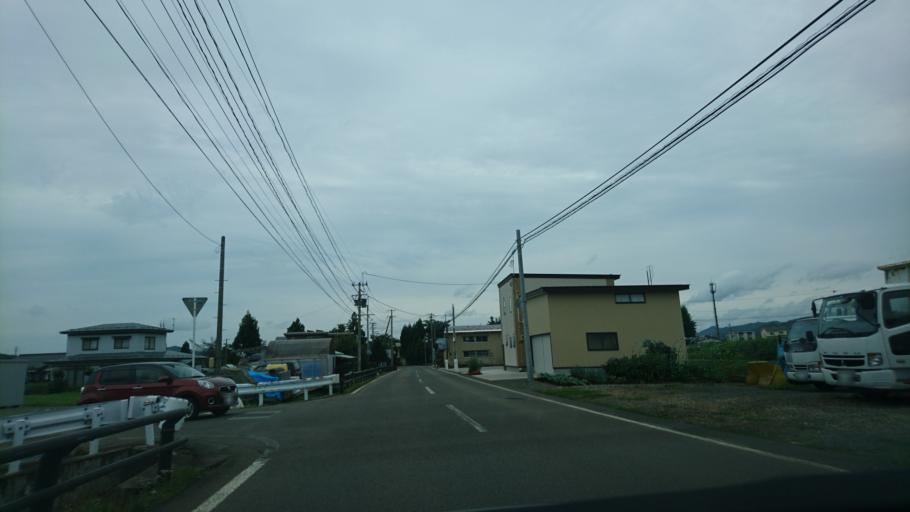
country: JP
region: Akita
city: Yuzawa
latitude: 39.1507
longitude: 140.5705
